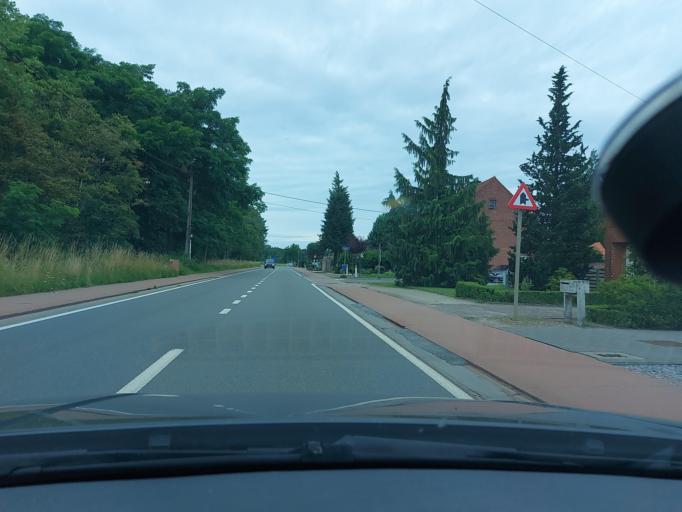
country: BE
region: Flanders
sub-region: Provincie Antwerpen
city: Balen
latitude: 51.2061
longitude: 5.2225
